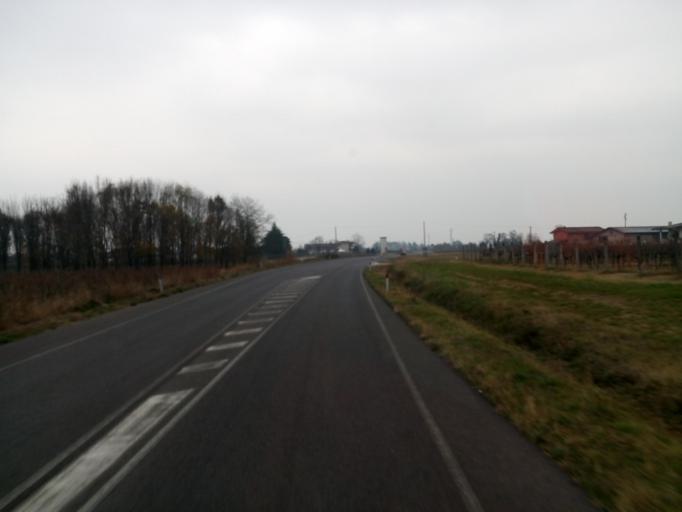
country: IT
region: Friuli Venezia Giulia
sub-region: Provincia di Udine
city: Buttrio
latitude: 46.0362
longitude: 13.3303
